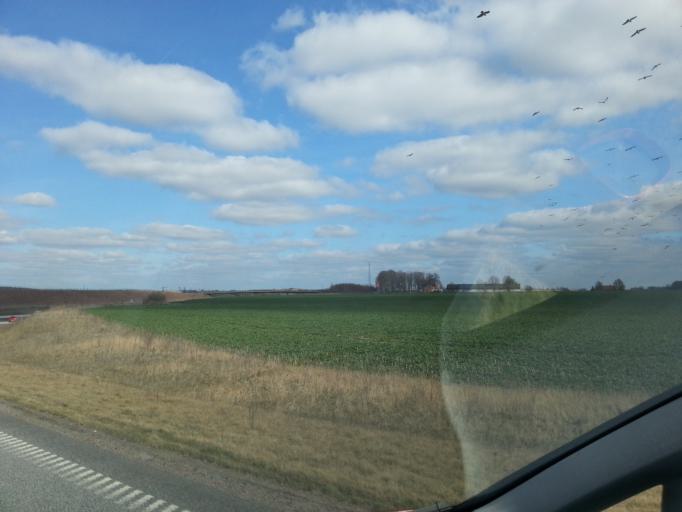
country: SE
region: Skane
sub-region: Malmo
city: Tygelsjo
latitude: 55.5453
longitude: 13.0045
